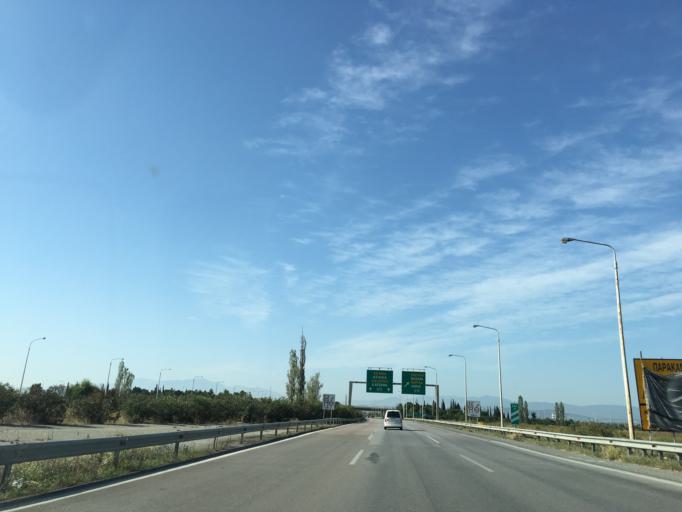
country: GR
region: Central Macedonia
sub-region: Nomos Imathias
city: Kleidi
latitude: 40.5600
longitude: 22.6029
